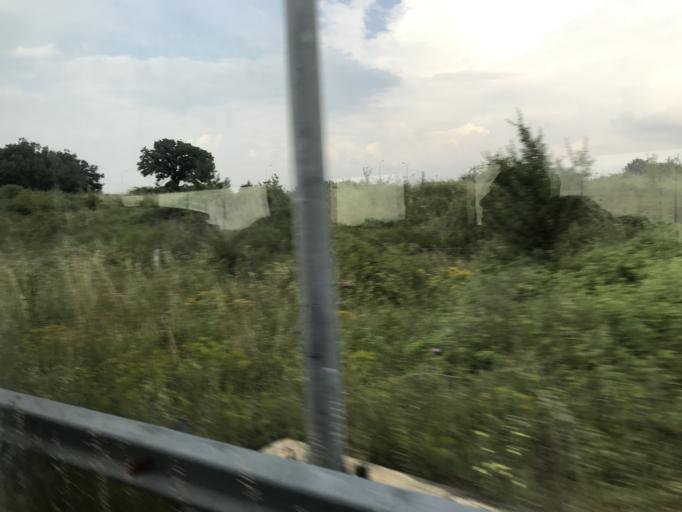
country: GR
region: East Macedonia and Thrace
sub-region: Nomos Rodopis
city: Sapes
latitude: 40.9614
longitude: 25.6434
